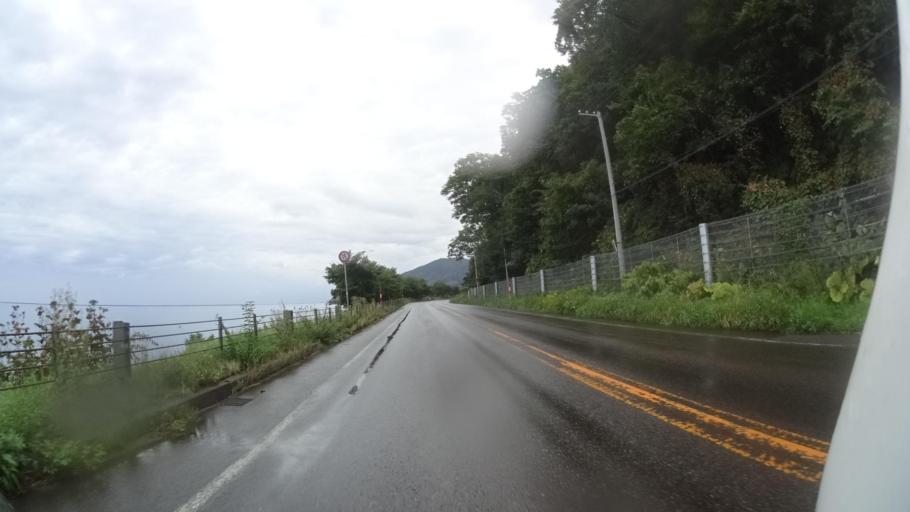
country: JP
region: Hokkaido
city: Kitami
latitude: 44.0967
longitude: 143.7859
